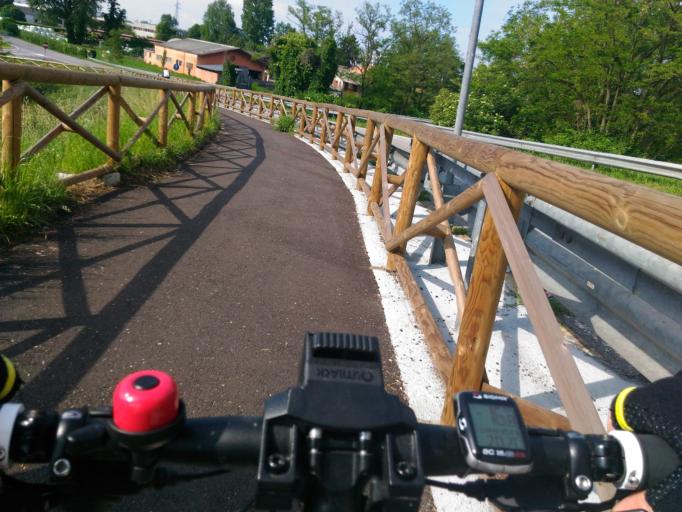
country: IT
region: Lombardy
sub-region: Provincia di Lodi
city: Montanaso Lombardo
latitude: 45.3220
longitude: 9.4589
